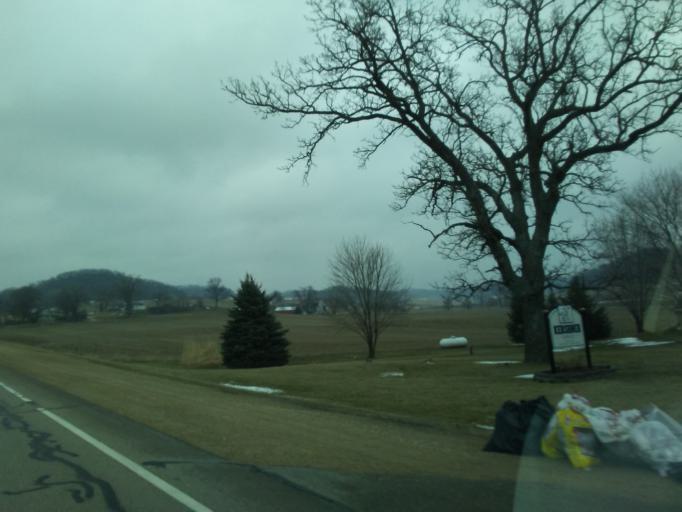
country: US
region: Wisconsin
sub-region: Richland County
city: Richland Center
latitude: 43.2464
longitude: -90.2914
